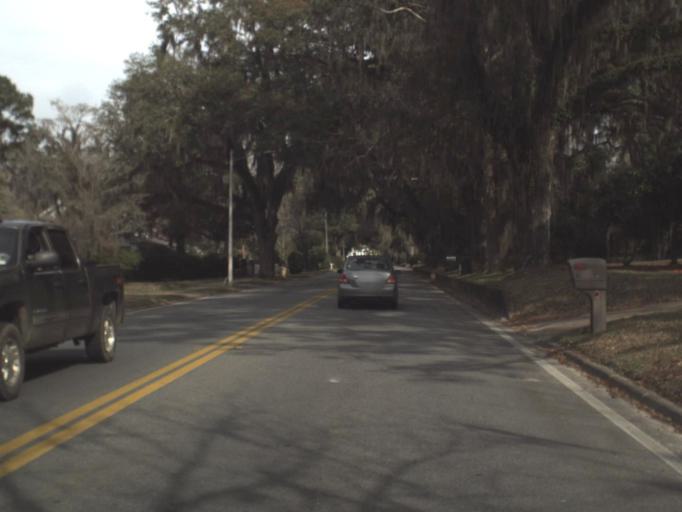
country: US
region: Florida
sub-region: Jefferson County
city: Monticello
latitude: 30.5452
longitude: -83.8774
